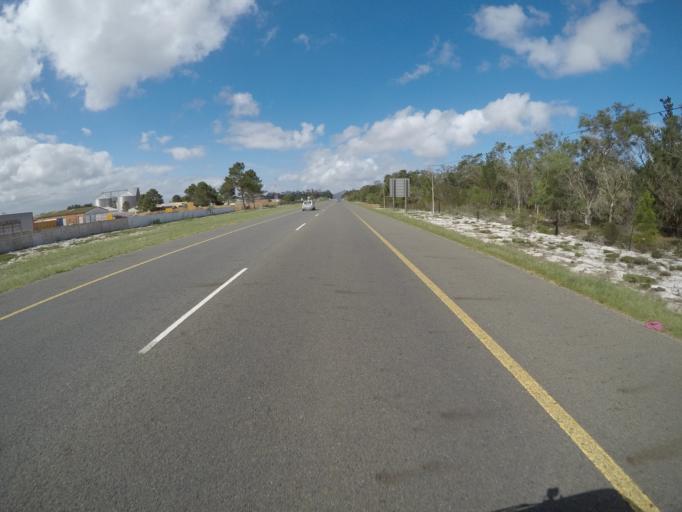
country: ZA
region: Western Cape
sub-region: Eden District Municipality
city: Riversdale
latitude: -34.2128
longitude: 21.5794
